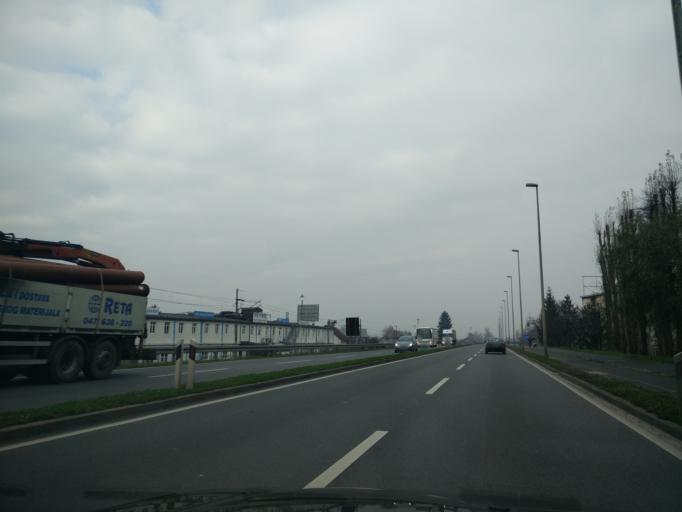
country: HR
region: Karlovacka
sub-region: Grad Karlovac
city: Karlovac
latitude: 45.4920
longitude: 15.5475
